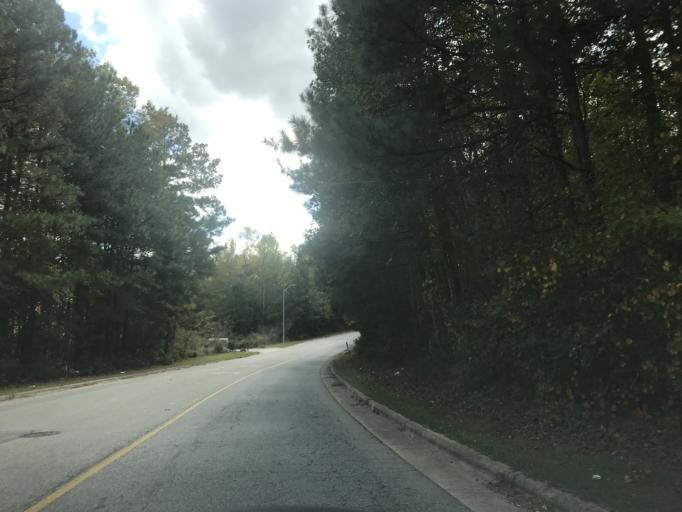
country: US
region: North Carolina
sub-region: Wake County
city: Garner
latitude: 35.7282
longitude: -78.6574
